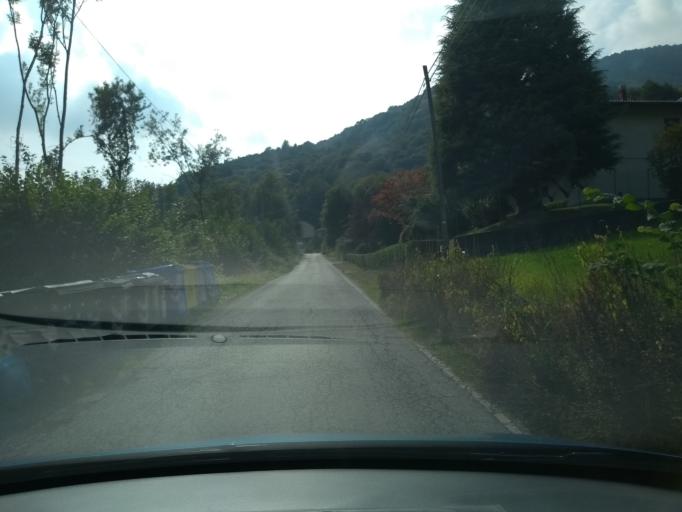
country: IT
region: Piedmont
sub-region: Provincia di Torino
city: Corio
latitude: 45.3149
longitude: 7.5215
